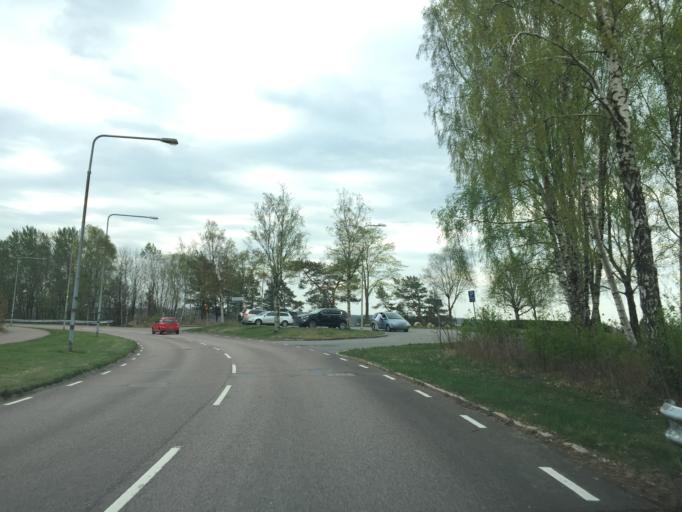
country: SE
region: Vaestra Goetaland
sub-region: Goteborg
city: Rannebergen
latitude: 57.7992
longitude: 12.0690
